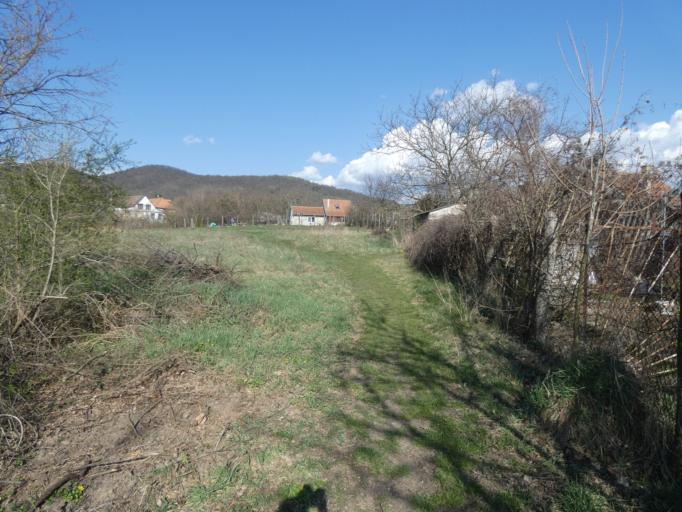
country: HU
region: Pest
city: Szob
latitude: 47.8657
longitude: 18.8759
